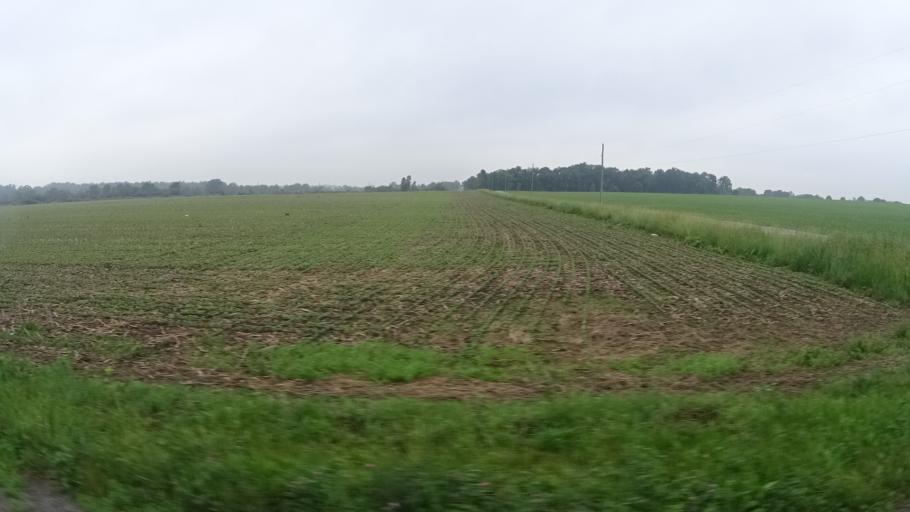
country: US
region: Ohio
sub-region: Erie County
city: Sandusky
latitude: 41.3614
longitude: -82.7697
